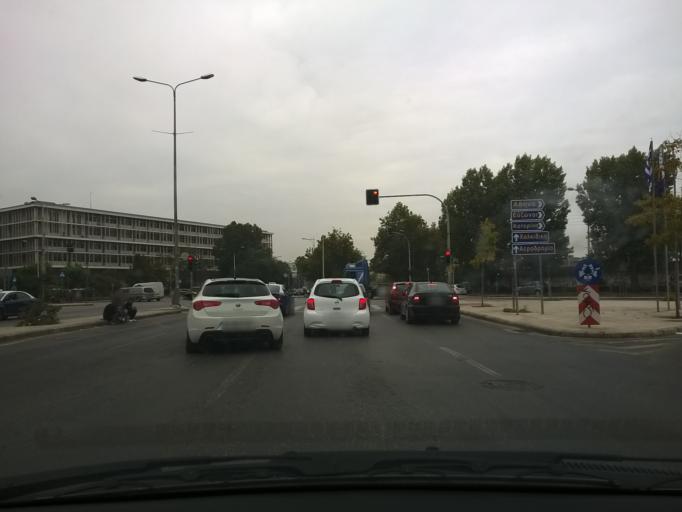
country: GR
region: Central Macedonia
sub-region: Nomos Thessalonikis
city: Thessaloniki
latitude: 40.6399
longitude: 22.9304
